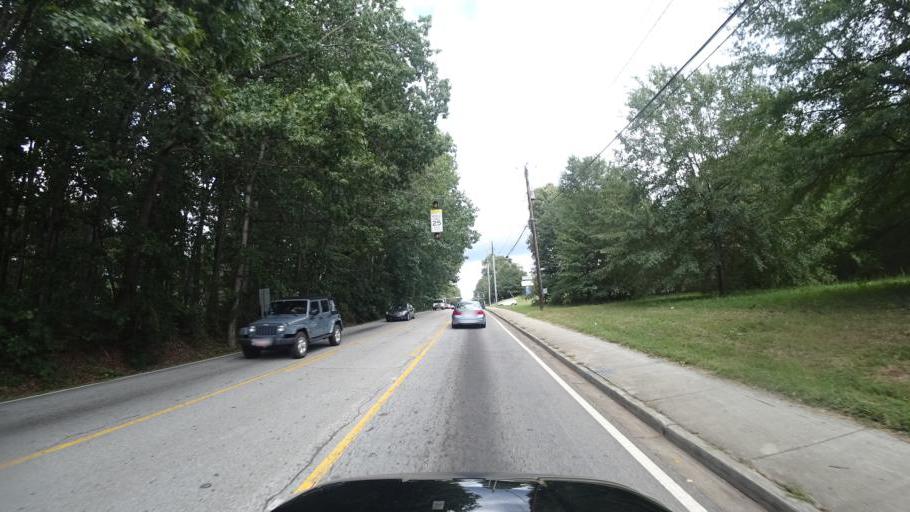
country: US
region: Georgia
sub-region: DeKalb County
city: Stone Mountain
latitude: 33.7598
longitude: -84.1806
